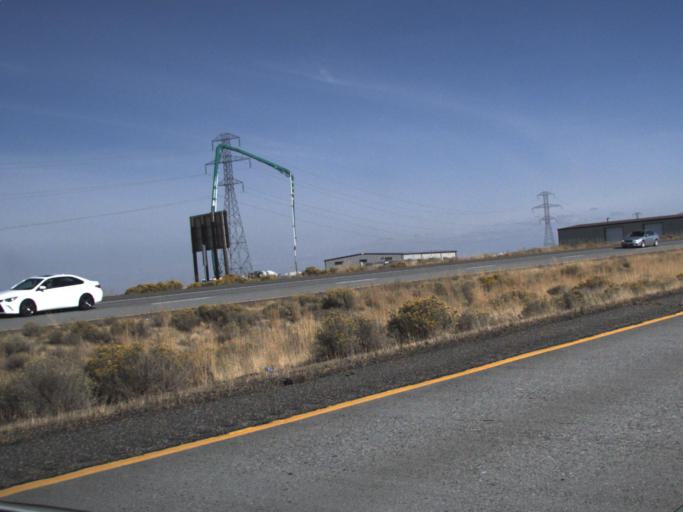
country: US
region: Washington
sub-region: Franklin County
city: West Pasco
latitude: 46.1727
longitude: -119.2111
